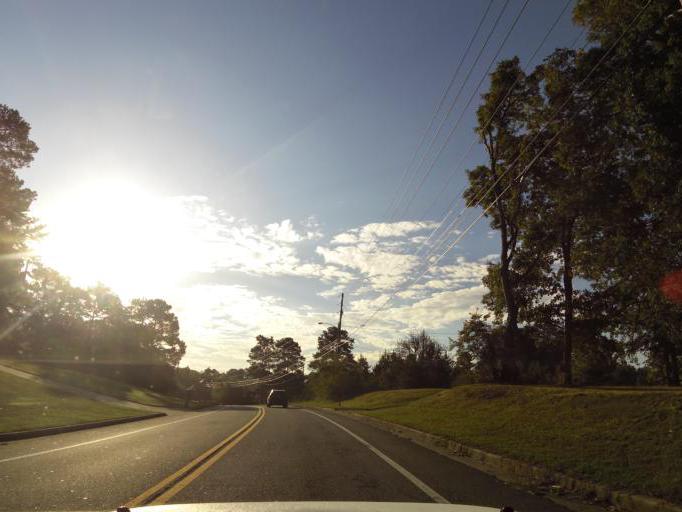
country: US
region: Georgia
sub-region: Cobb County
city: Kennesaw
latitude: 33.9945
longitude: -84.6400
